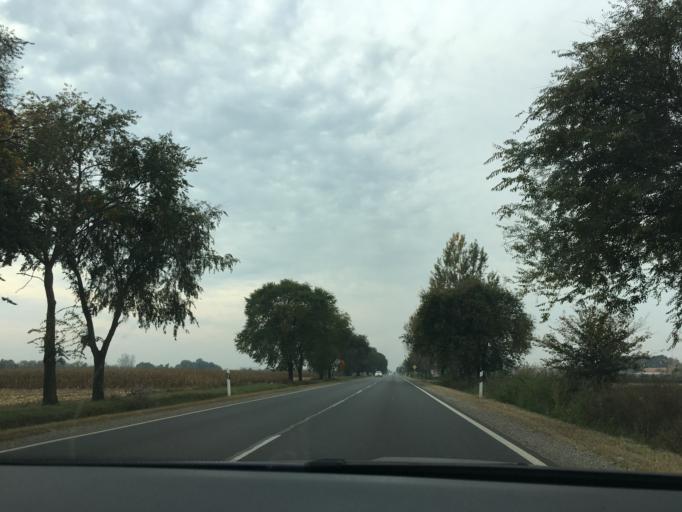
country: HU
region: Hajdu-Bihar
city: Kaba
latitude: 47.3828
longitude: 21.2829
